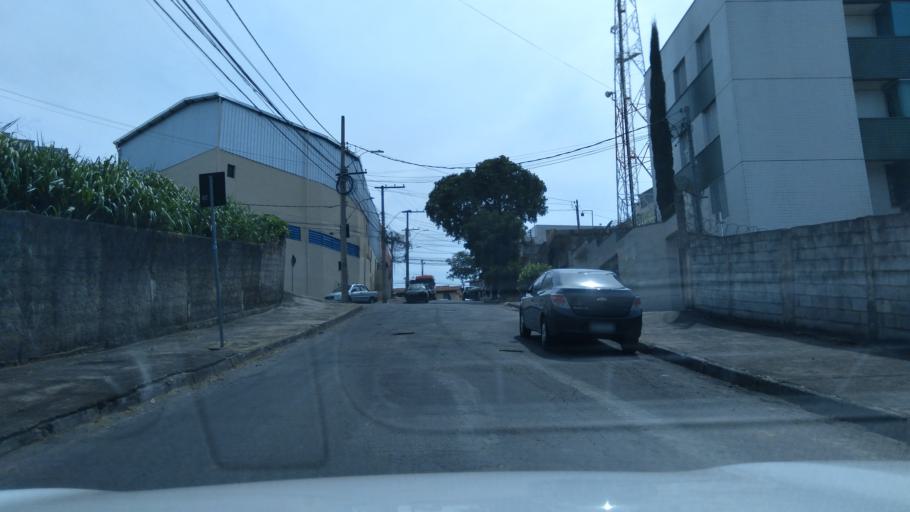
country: BR
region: Minas Gerais
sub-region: Contagem
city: Contagem
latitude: -19.8988
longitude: -44.0068
